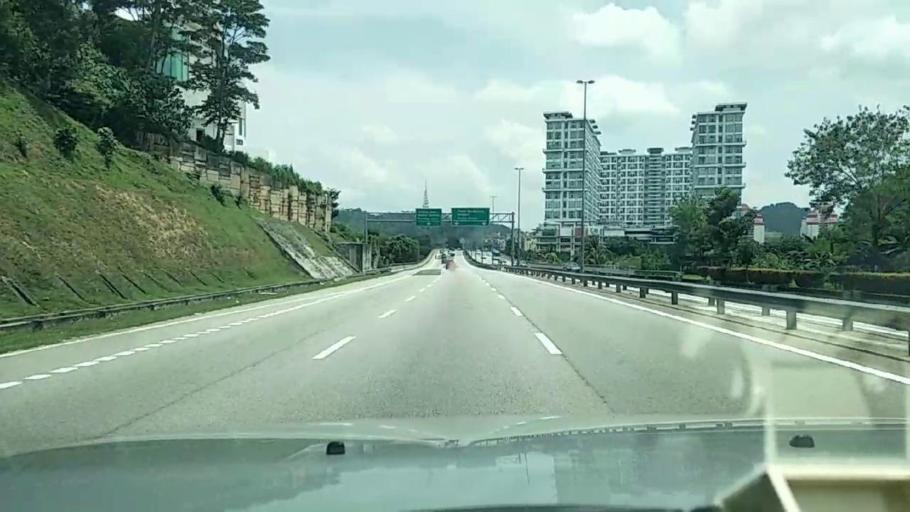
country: MY
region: Kuala Lumpur
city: Kuala Lumpur
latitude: 3.0941
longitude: 101.6788
